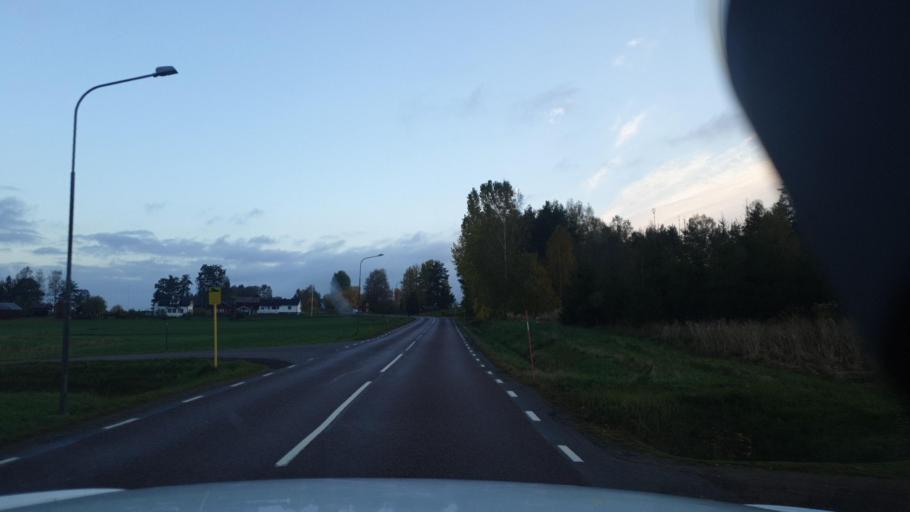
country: SE
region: Vaermland
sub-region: Arvika Kommun
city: Arvika
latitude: 59.7779
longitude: 12.5504
